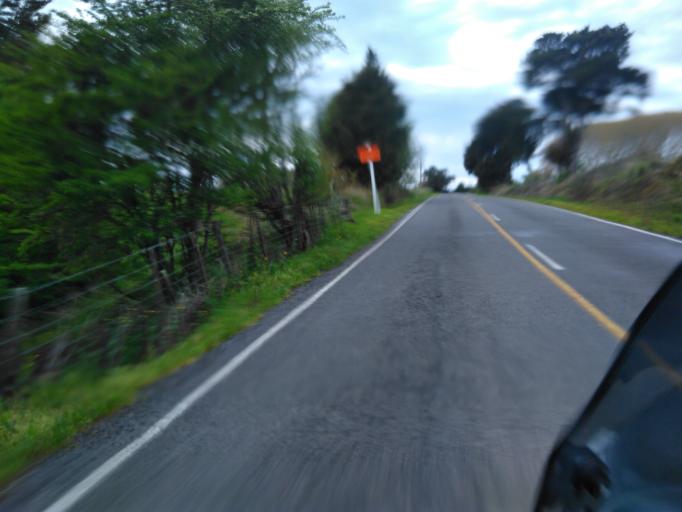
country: NZ
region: Hawke's Bay
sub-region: Wairoa District
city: Wairoa
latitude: -38.8957
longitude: 177.4556
